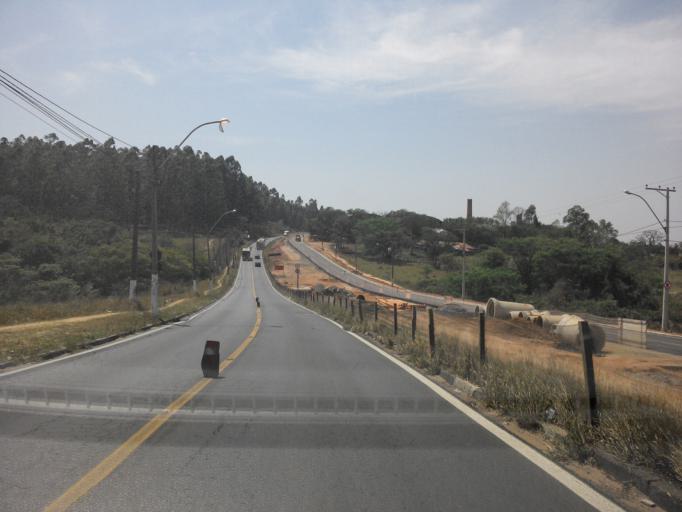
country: BR
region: Sao Paulo
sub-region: Hortolandia
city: Hortolandia
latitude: -22.9410
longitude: -47.1704
